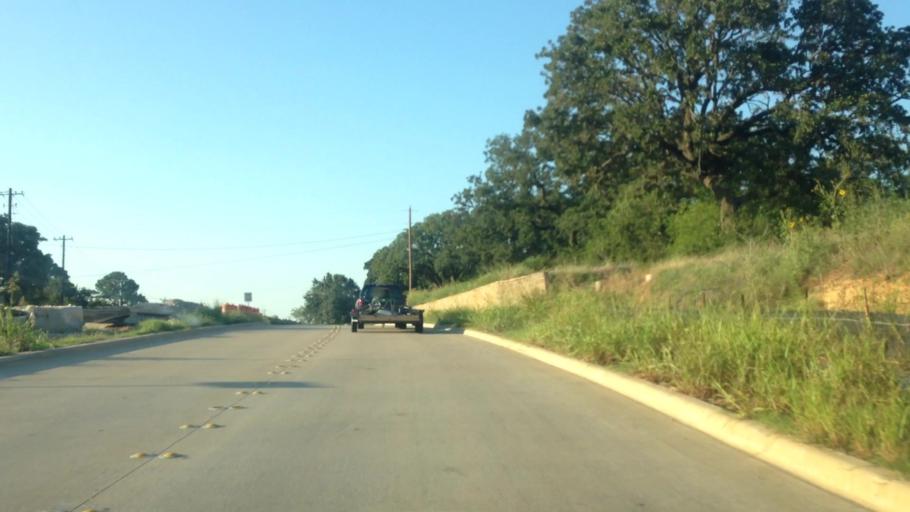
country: US
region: Texas
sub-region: Denton County
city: Trophy Club
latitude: 32.9597
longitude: -97.1860
